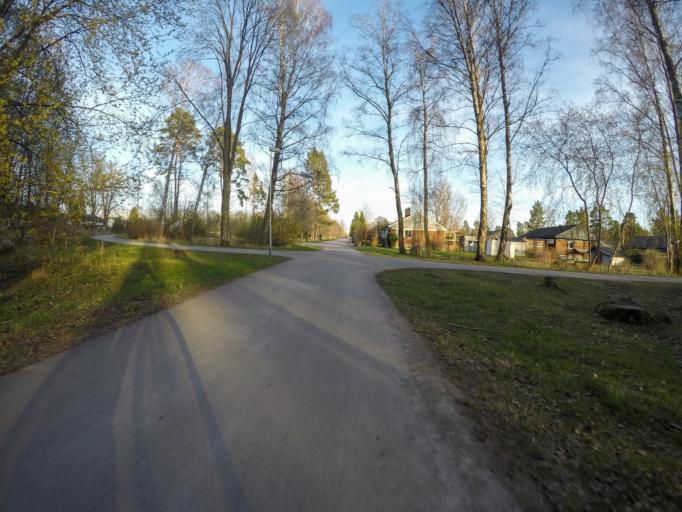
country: SE
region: Vaestmanland
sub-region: Vasteras
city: Vasteras
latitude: 59.5964
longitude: 16.6065
